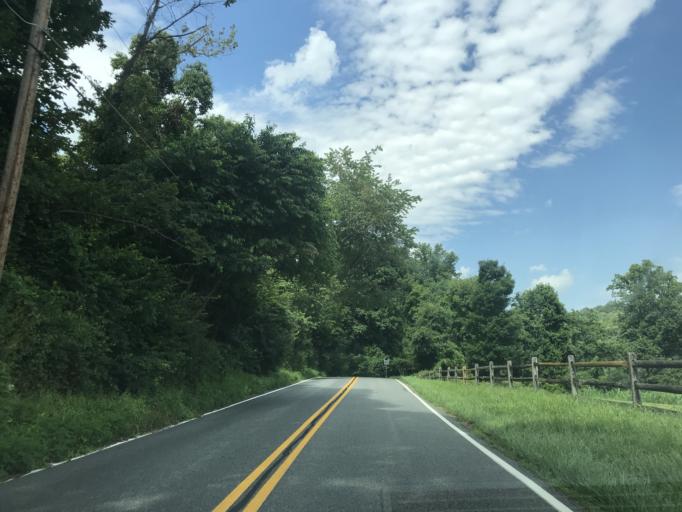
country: US
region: Delaware
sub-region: New Castle County
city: Greenville
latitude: 39.8432
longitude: -75.5714
